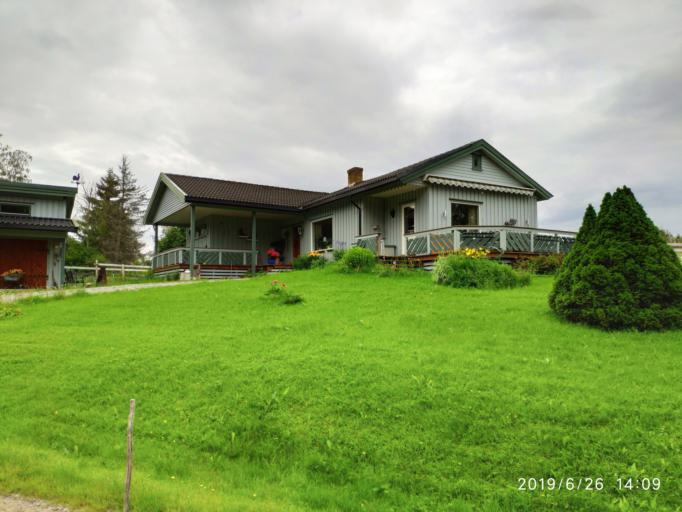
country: NO
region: Hedmark
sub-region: Loten
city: Loten
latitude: 60.8327
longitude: 11.3896
